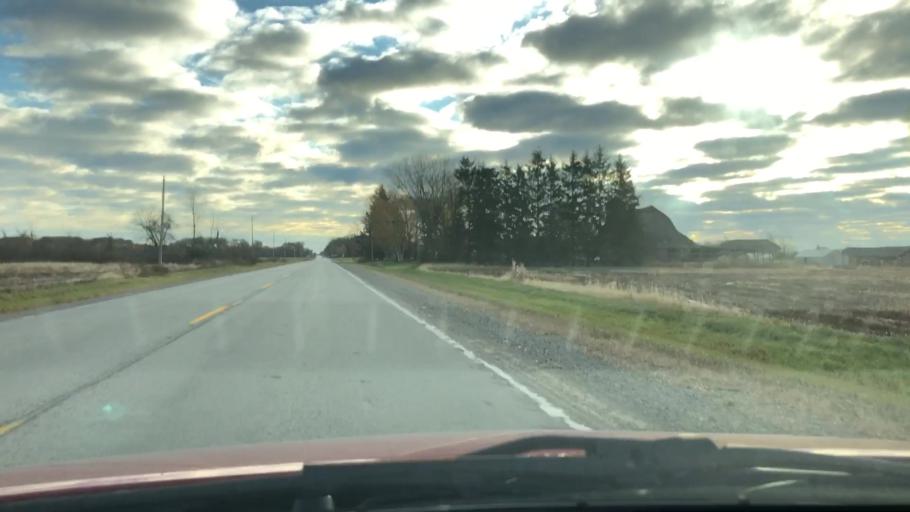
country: US
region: Wisconsin
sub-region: Brown County
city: Oneida
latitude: 44.4442
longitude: -88.1975
